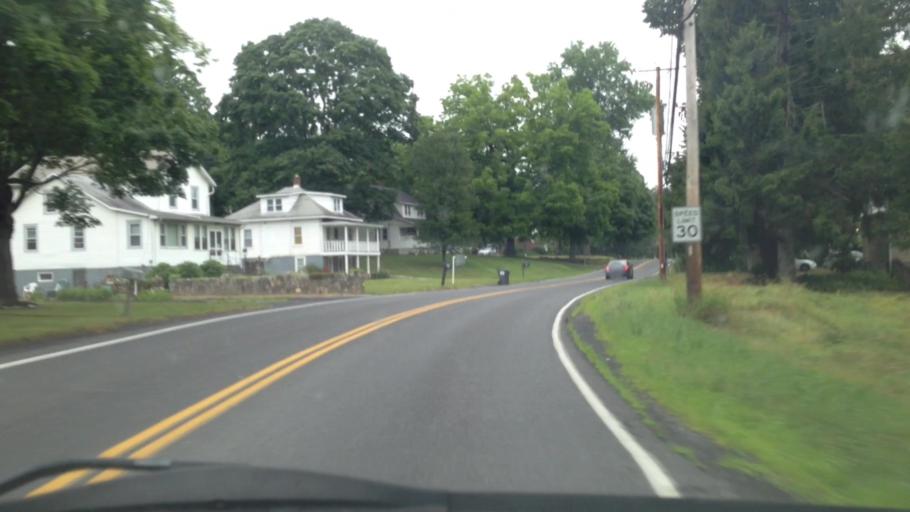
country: US
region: New York
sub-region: Ulster County
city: Highland
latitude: 41.7252
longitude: -73.9684
